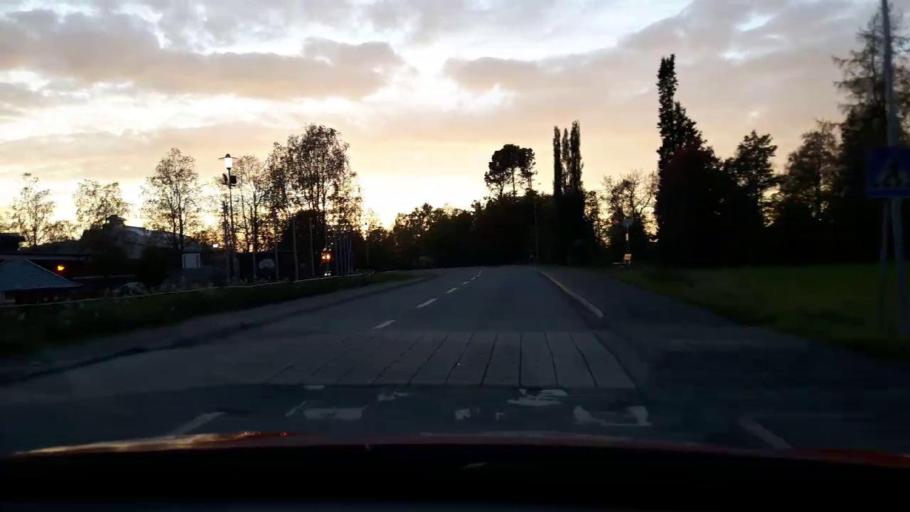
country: SE
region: Jaemtland
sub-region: OEstersunds Kommun
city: Ostersund
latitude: 63.2479
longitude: 14.5679
